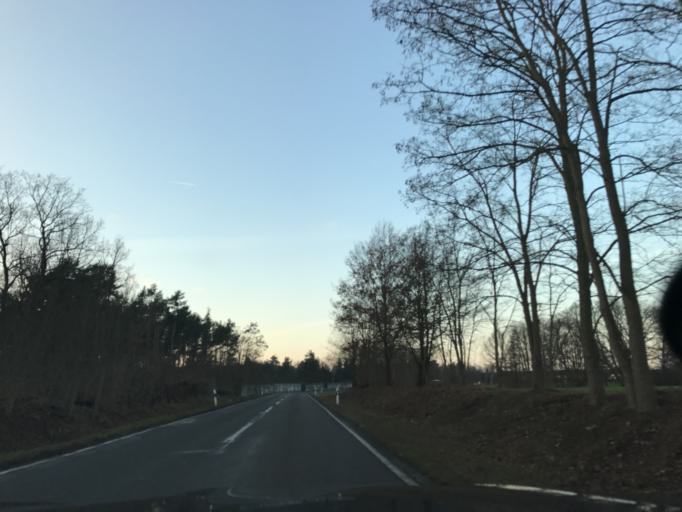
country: DE
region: Brandenburg
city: Wusterwitz
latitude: 52.4319
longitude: 12.4308
